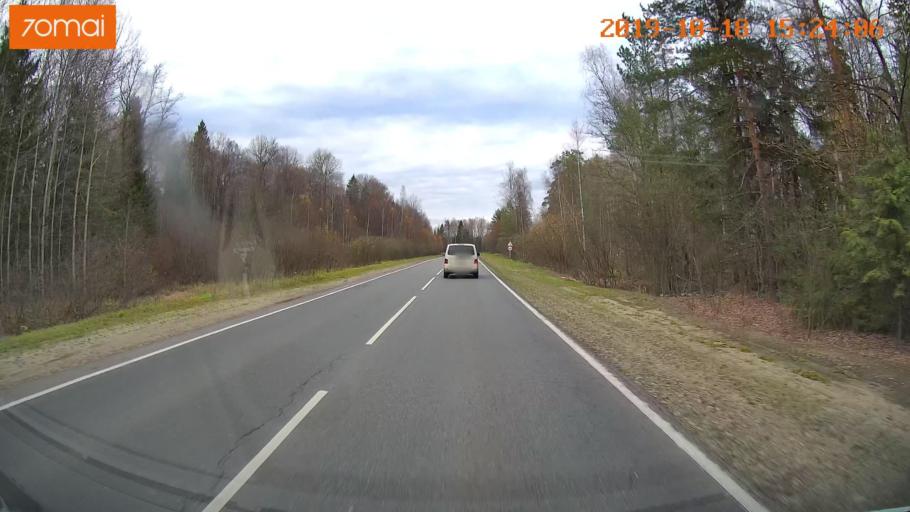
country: RU
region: Vladimir
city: Anopino
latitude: 55.7303
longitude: 40.7253
